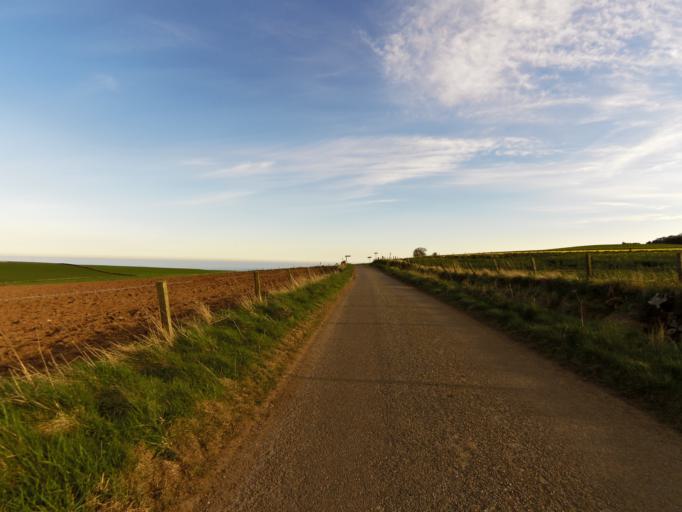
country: GB
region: Scotland
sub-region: Aberdeenshire
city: Inverbervie
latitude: 56.8792
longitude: -2.2356
